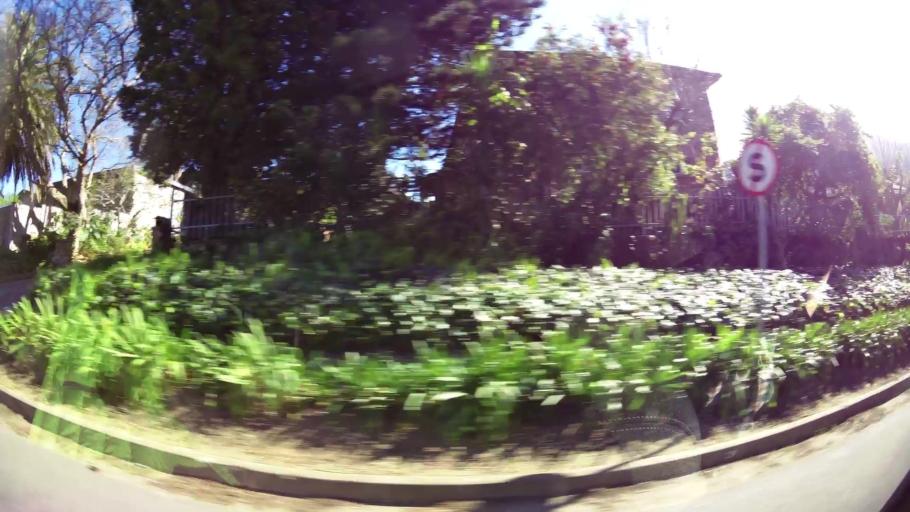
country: ZA
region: Western Cape
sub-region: Eden District Municipality
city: George
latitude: -33.9472
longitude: 22.4683
